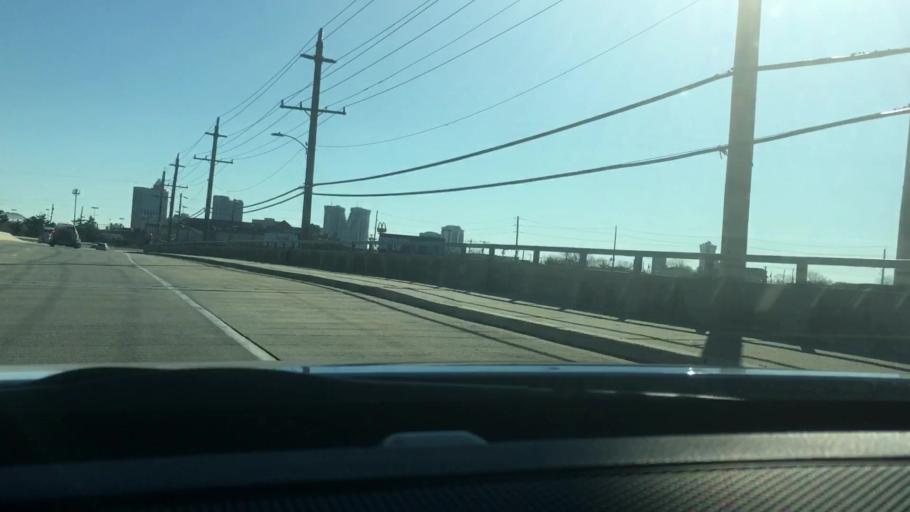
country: US
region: New Jersey
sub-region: Atlantic County
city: Ventnor City
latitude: 39.3614
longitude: -74.4648
